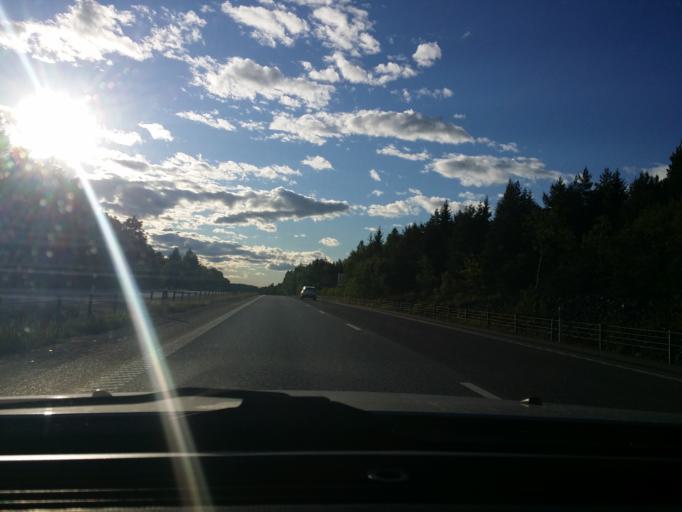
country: SE
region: Uppsala
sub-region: Habo Kommun
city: Balsta
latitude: 59.5608
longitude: 17.5723
